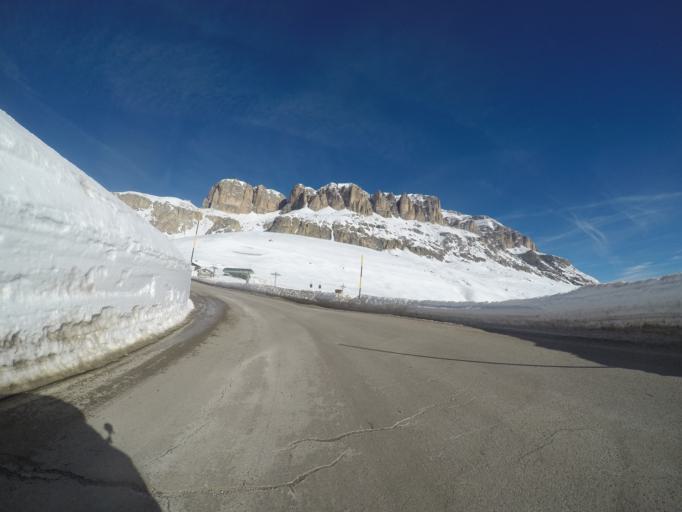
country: IT
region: Trentino-Alto Adige
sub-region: Provincia di Trento
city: Canazei
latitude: 46.4860
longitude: 11.8162
